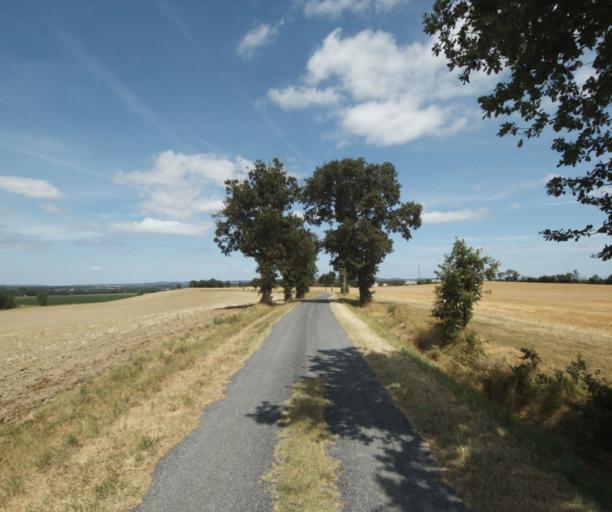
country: FR
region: Midi-Pyrenees
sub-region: Departement du Tarn
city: Dourgne
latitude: 43.4946
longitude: 2.1016
